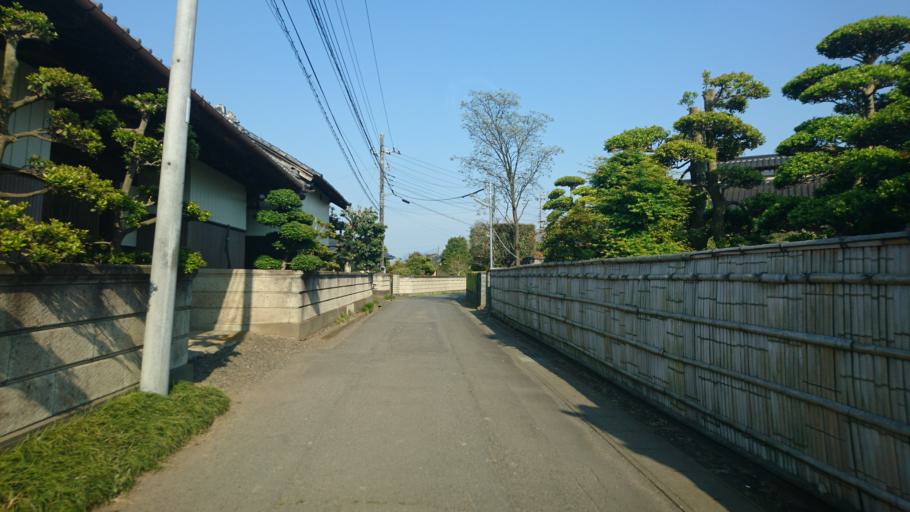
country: JP
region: Ibaraki
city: Yuki
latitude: 36.2496
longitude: 139.9173
